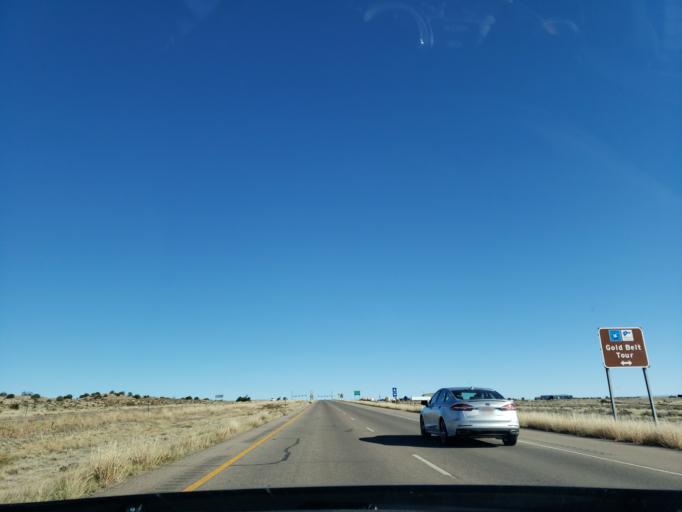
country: US
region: Colorado
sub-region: Fremont County
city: Florence
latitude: 38.4390
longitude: -105.1208
